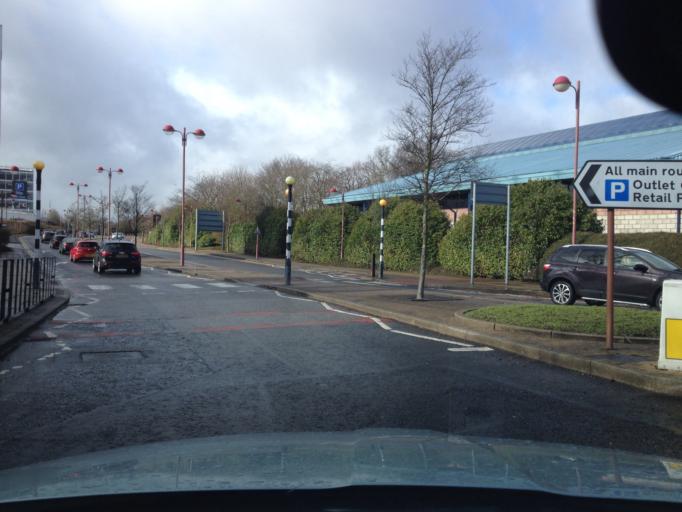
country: GB
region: Scotland
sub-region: West Lothian
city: Livingston
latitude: 55.8841
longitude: -3.5188
